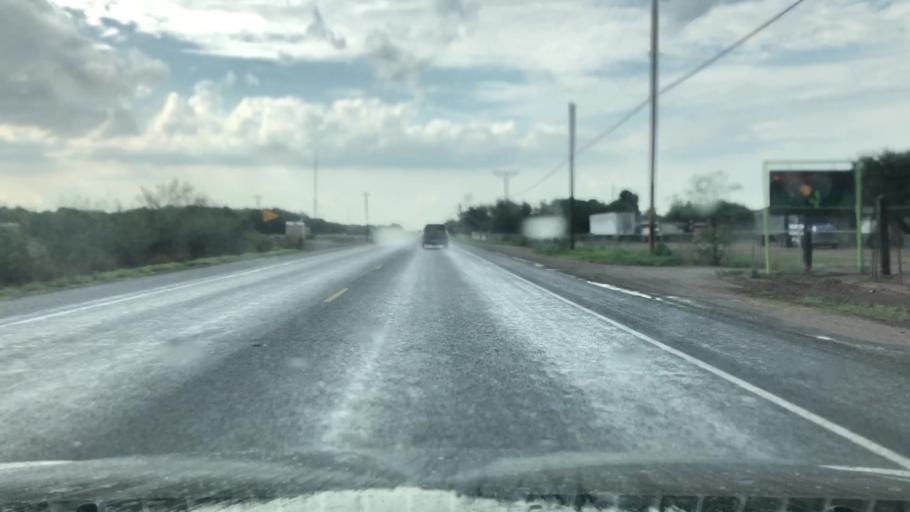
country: US
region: New Mexico
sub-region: Dona Ana County
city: Mesquite
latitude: 32.1907
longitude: -106.7131
